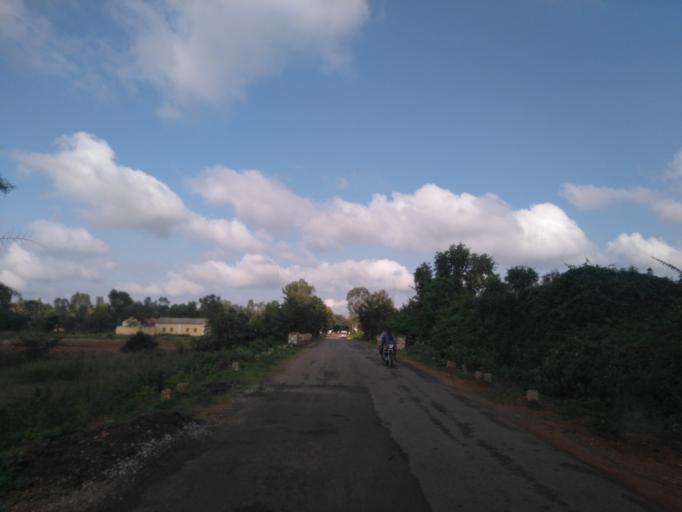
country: IN
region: Karnataka
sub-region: Mysore
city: Tirumakudal Narsipur
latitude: 12.2572
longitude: 76.9649
